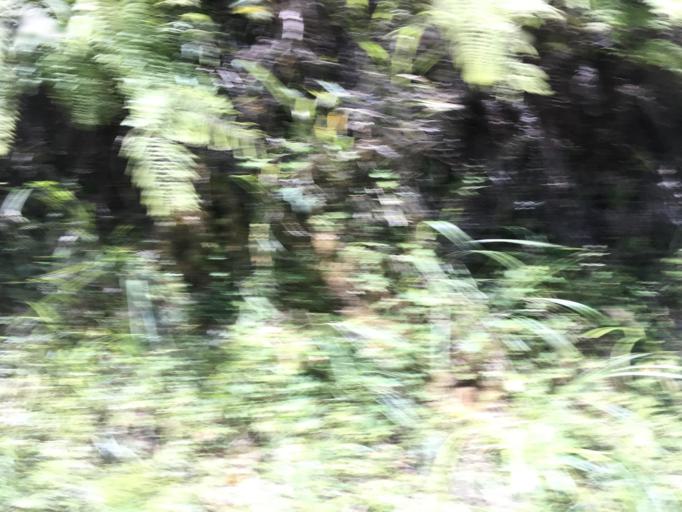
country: TW
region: Taiwan
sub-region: Yilan
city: Yilan
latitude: 24.5211
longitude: 121.5205
